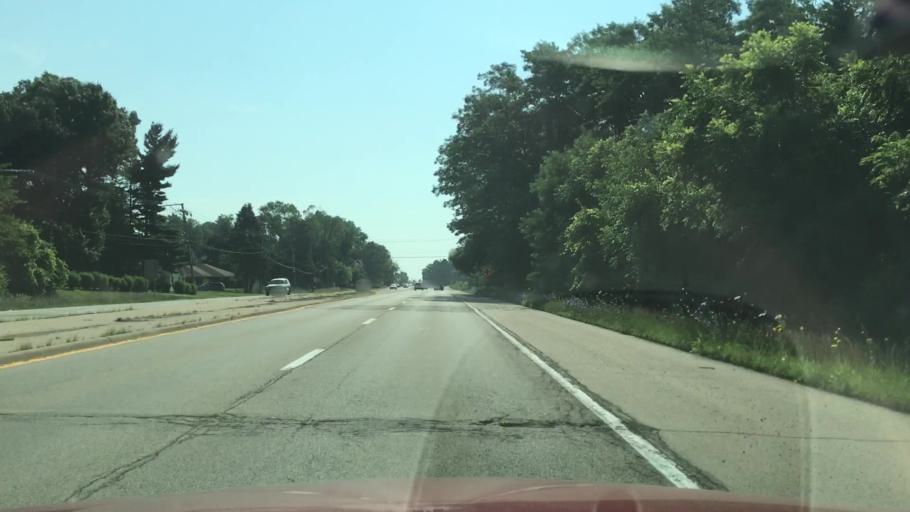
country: US
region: Illinois
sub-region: Winnebago County
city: Cherry Valley
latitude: 42.2385
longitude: -88.9909
